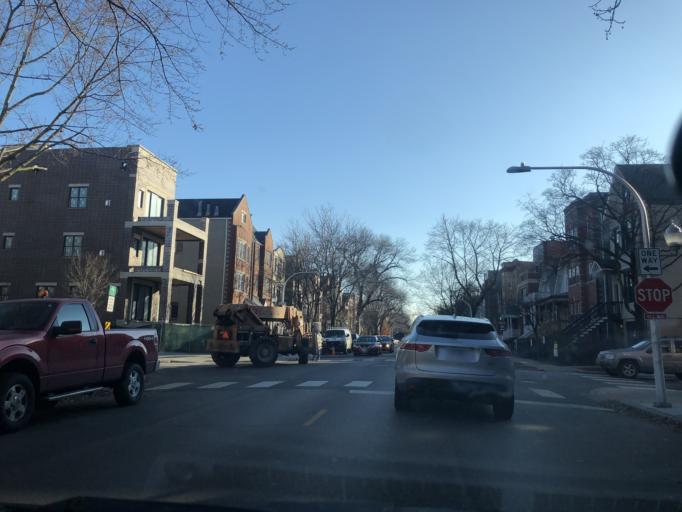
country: US
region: Illinois
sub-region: Cook County
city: Chicago
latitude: 41.9420
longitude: -87.6591
